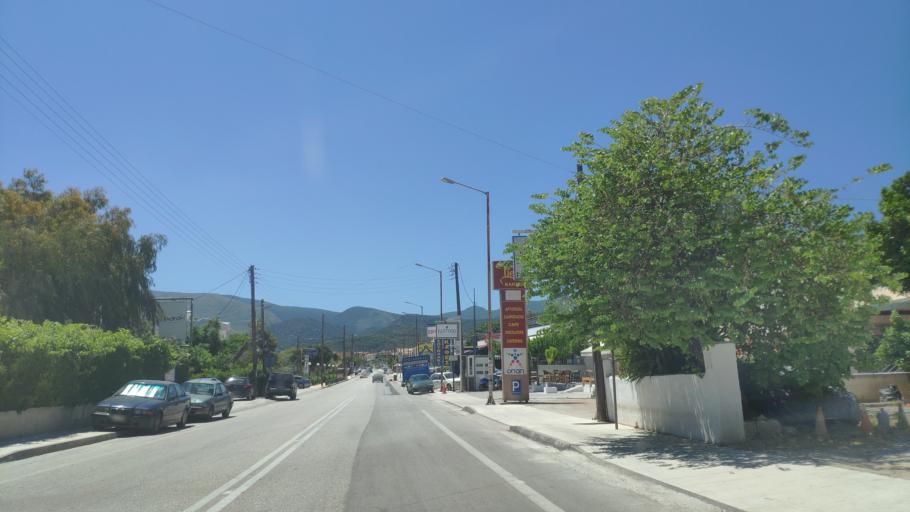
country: GR
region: Peloponnese
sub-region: Nomos Korinthias
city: Loutra Oraias Elenis
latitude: 37.8653
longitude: 22.9971
